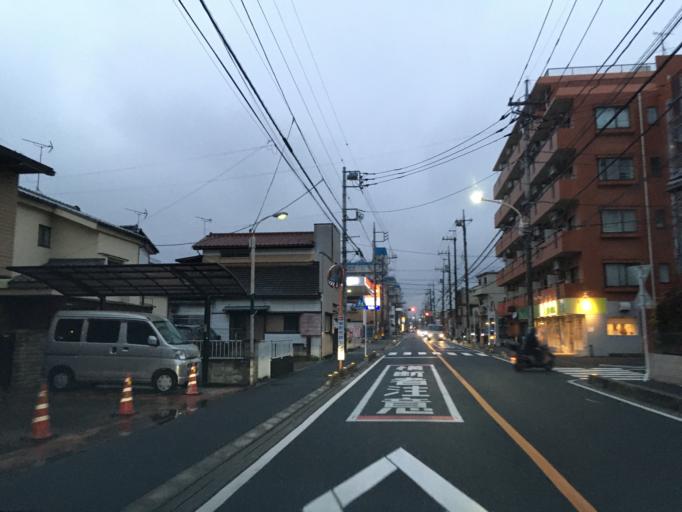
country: JP
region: Saitama
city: Asaka
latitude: 35.7857
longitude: 139.6019
